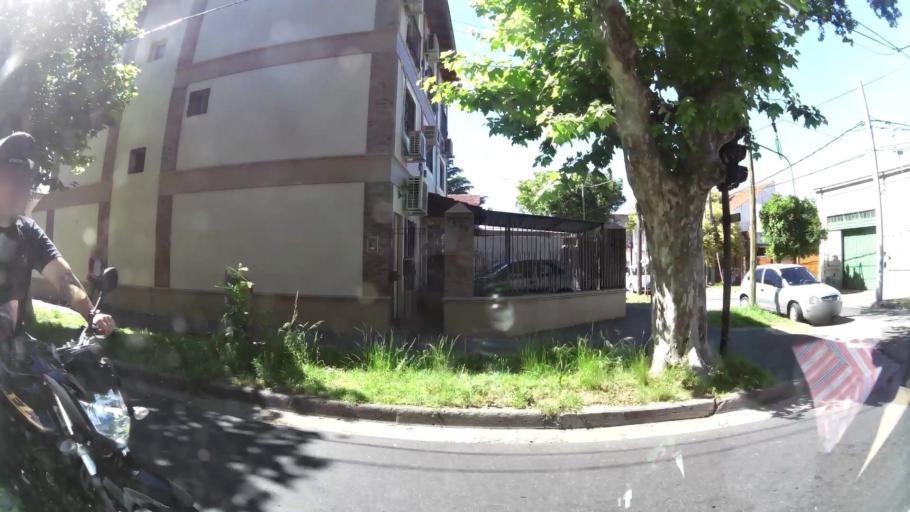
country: AR
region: Buenos Aires
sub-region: Partido de General San Martin
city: General San Martin
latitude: -34.5350
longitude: -58.5269
